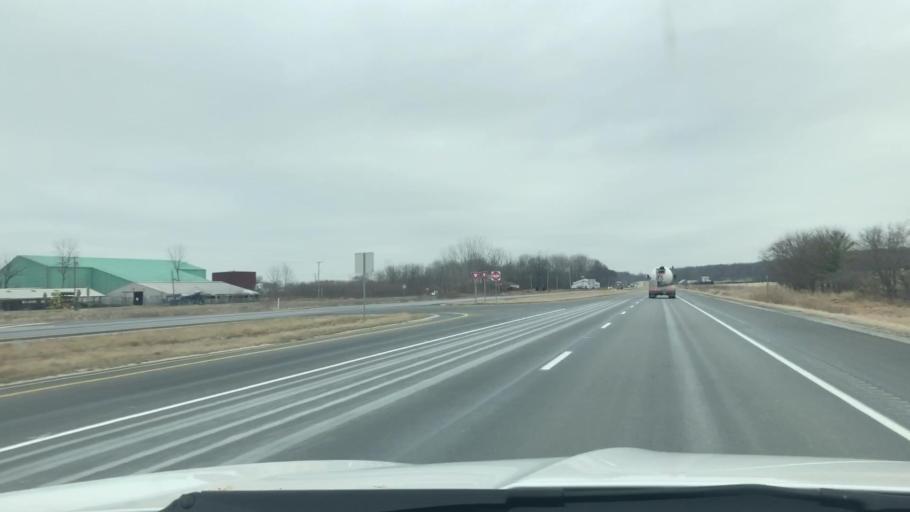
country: US
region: Indiana
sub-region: Cass County
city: Logansport
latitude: 40.7338
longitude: -86.3395
